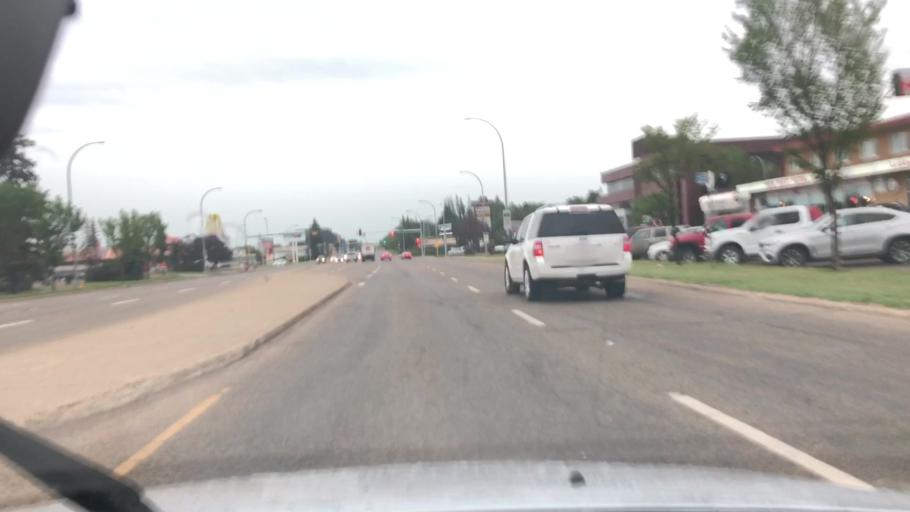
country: CA
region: Alberta
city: St. Albert
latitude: 53.5589
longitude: -113.5808
